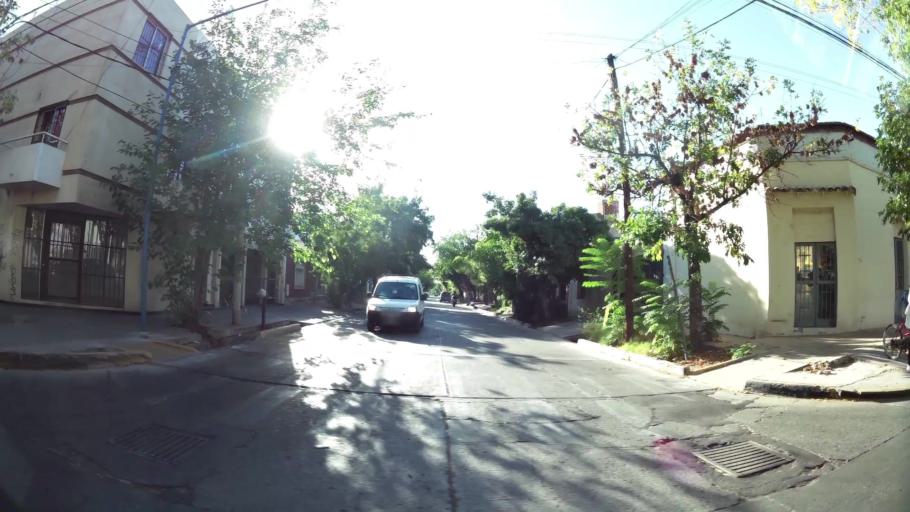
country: AR
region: Mendoza
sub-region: Departamento de Godoy Cruz
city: Godoy Cruz
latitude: -32.9333
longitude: -68.8461
